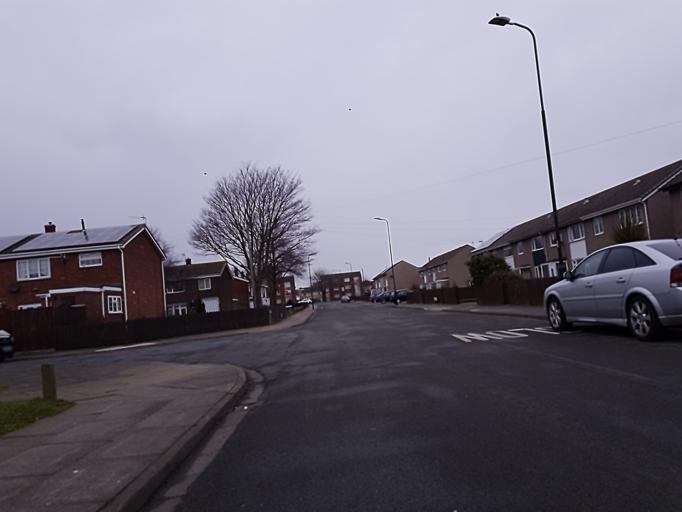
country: GB
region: England
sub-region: North East Lincolnshire
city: Great Coates
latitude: 53.5694
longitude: -0.1245
